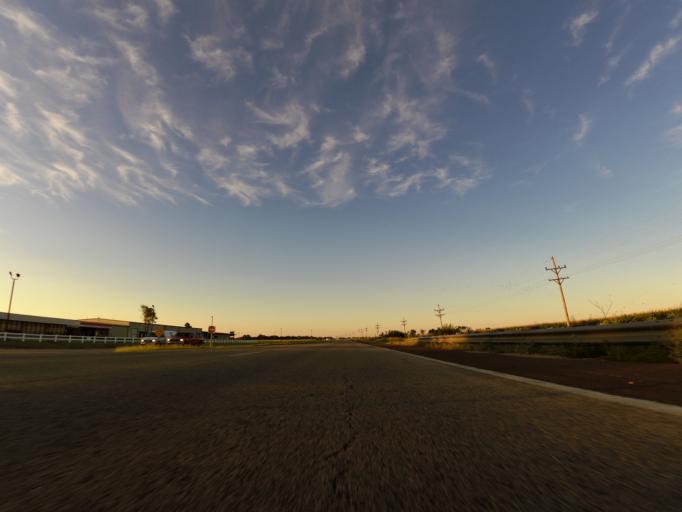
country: US
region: Kansas
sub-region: Reno County
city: South Hutchinson
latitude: 38.0032
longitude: -97.9406
